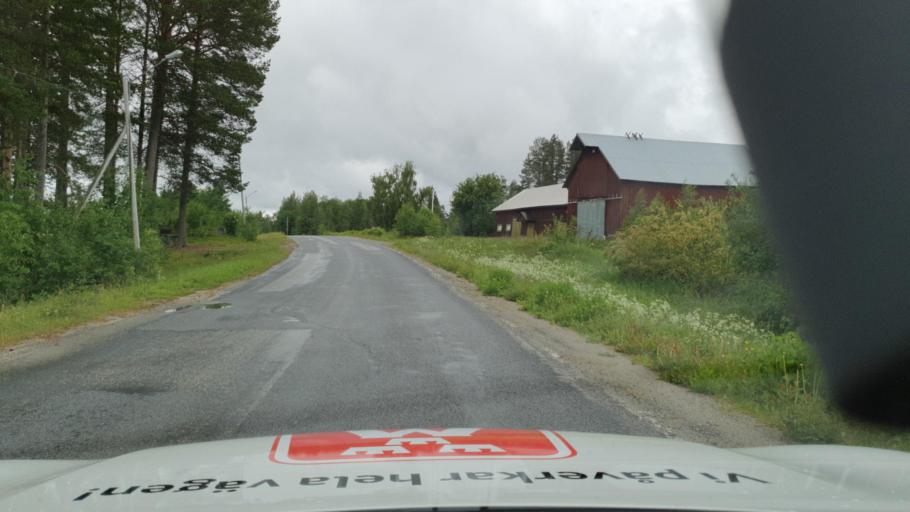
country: SE
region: Vaesterbotten
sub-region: Dorotea Kommun
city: Dorotea
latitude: 64.1106
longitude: 16.6405
